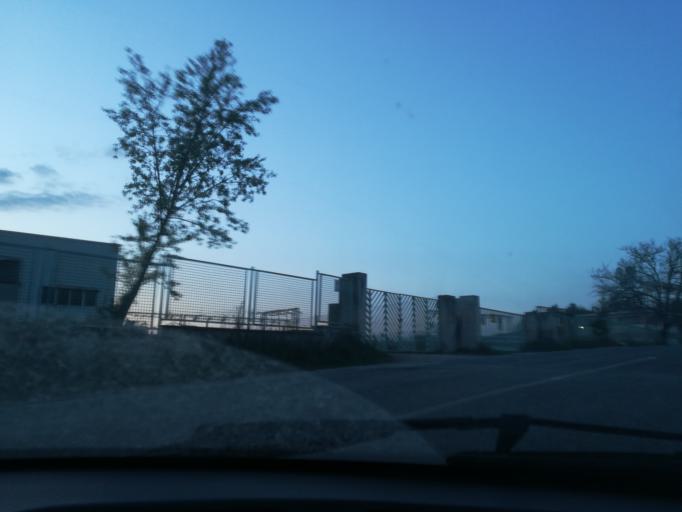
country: IT
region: The Marches
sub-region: Provincia di Macerata
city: Macerata
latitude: 43.2811
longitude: 13.4474
